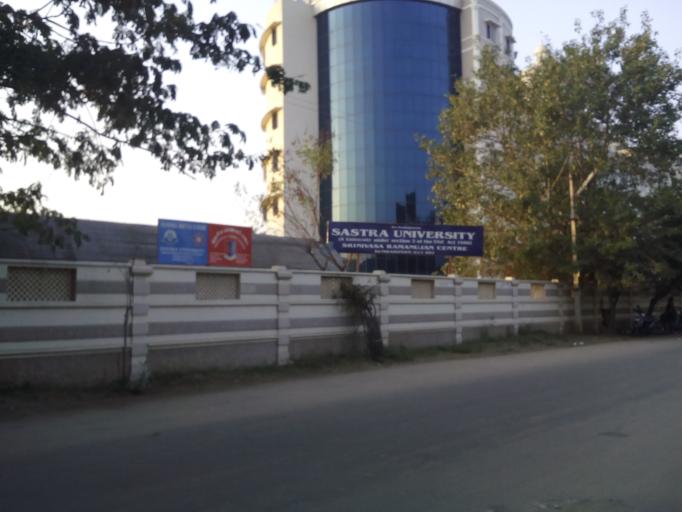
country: IN
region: Tamil Nadu
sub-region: Thanjavur
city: Kumbakonam
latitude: 10.9627
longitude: 79.3862
